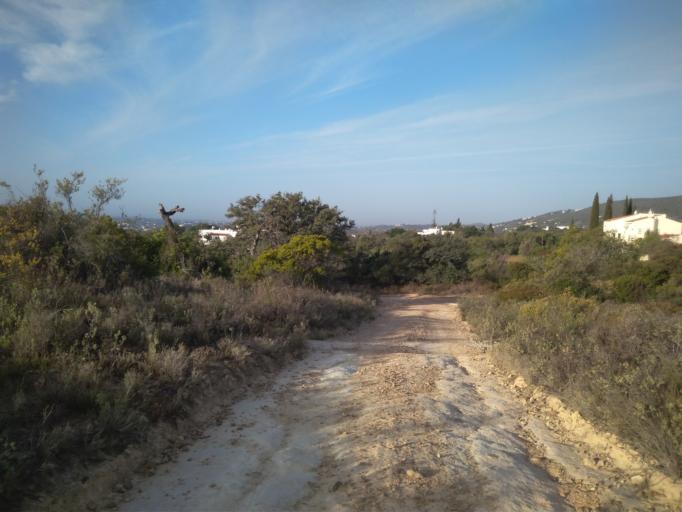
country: PT
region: Faro
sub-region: Faro
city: Santa Barbara de Nexe
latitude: 37.1004
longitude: -7.9579
